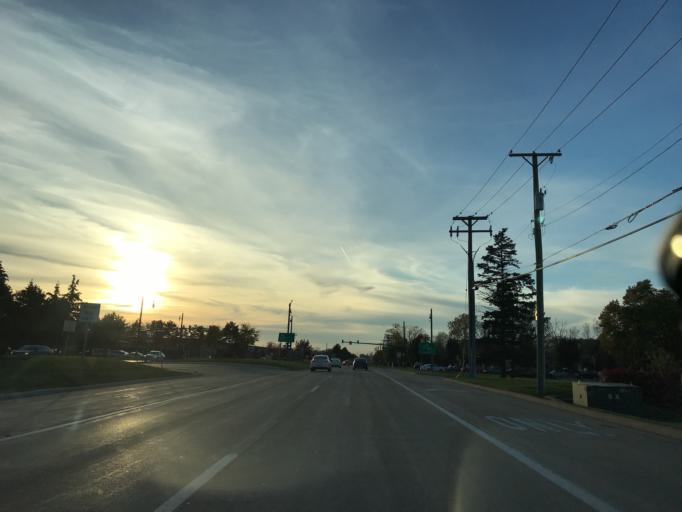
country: US
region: Michigan
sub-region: Oakland County
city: Novi
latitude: 42.4957
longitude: -83.4747
